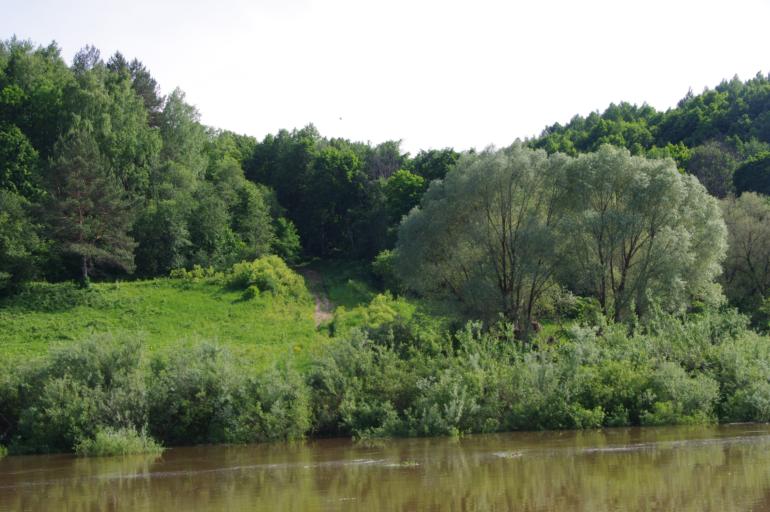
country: RU
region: Kaluga
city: Ferzikovo
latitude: 54.4195
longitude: 36.6113
